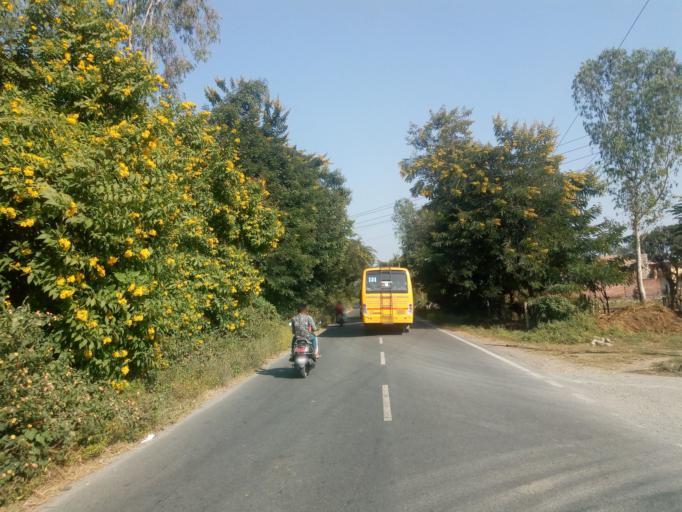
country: IN
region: Uttarakhand
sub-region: Dehradun
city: Harbatpur
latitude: 30.4416
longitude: 77.6972
